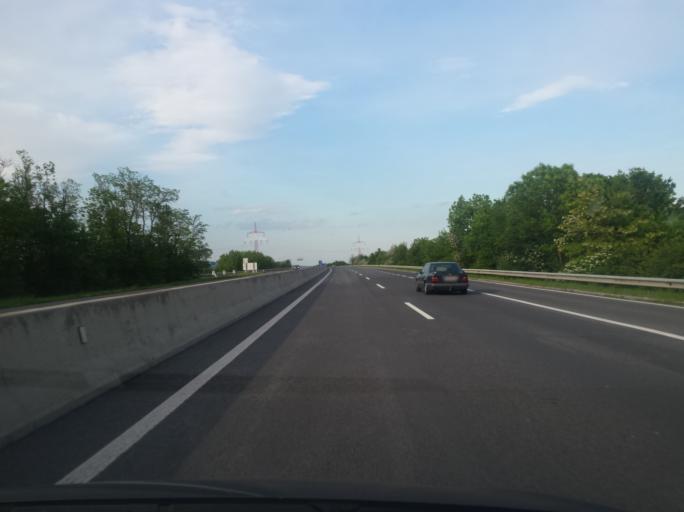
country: AT
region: Burgenland
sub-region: Politischer Bezirk Mattersburg
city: Hirm
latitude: 47.8027
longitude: 16.4717
